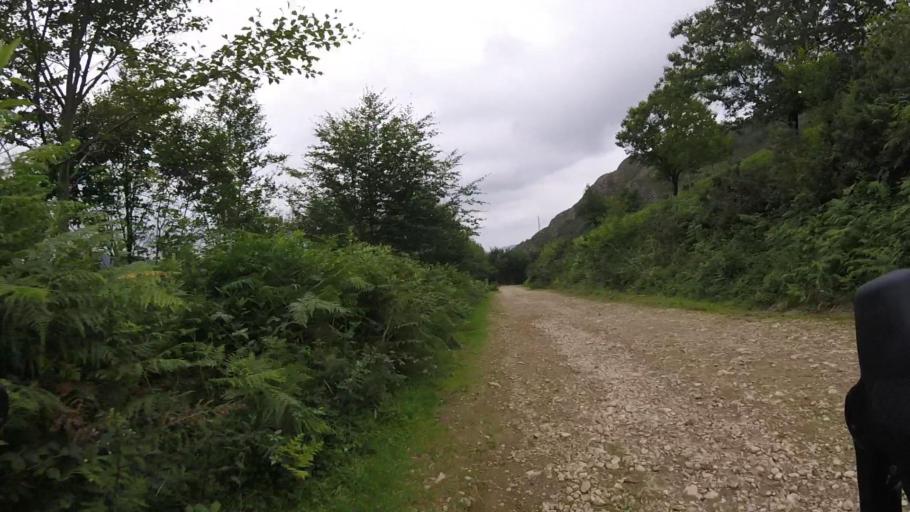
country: ES
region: Basque Country
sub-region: Provincia de Guipuzcoa
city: Irun
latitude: 43.2710
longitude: -1.7933
